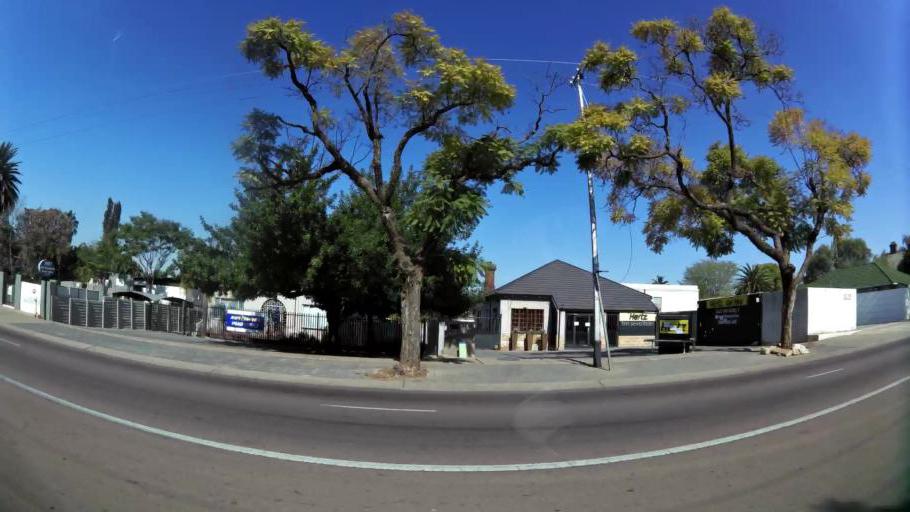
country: ZA
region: Gauteng
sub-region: City of Tshwane Metropolitan Municipality
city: Pretoria
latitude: -25.7435
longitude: 28.2309
